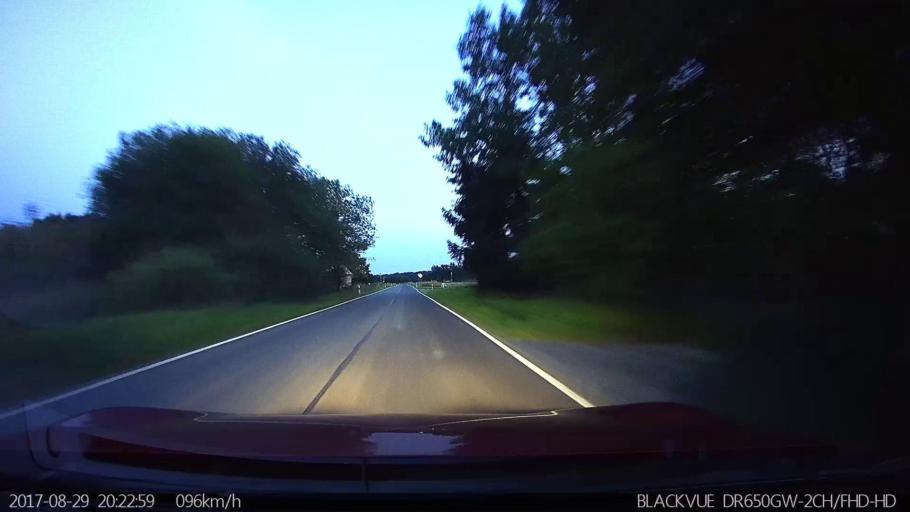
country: DE
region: Mecklenburg-Vorpommern
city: Velgast
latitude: 54.2305
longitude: 12.8265
